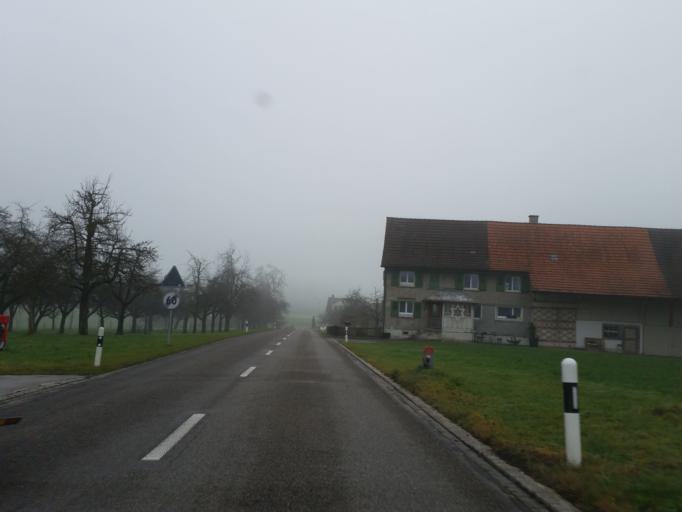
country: CH
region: Saint Gallen
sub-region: Wahlkreis Wil
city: Niederhelfenschwil
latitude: 47.5009
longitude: 9.1931
